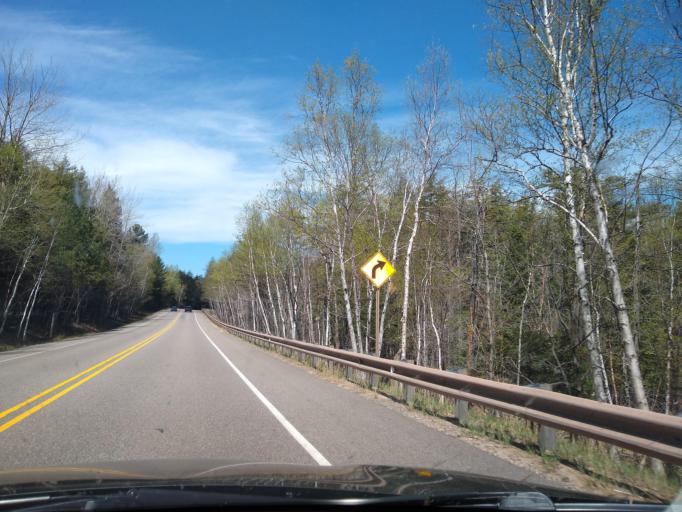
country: US
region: Michigan
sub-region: Marquette County
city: Trowbridge Park
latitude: 46.6217
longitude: -87.4683
